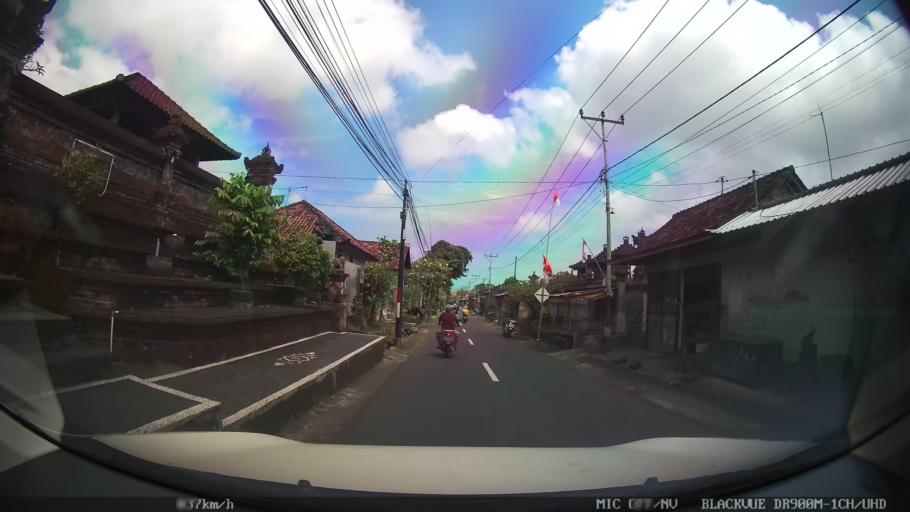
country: ID
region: Bali
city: Klungkung
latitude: -8.5302
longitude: 115.3832
